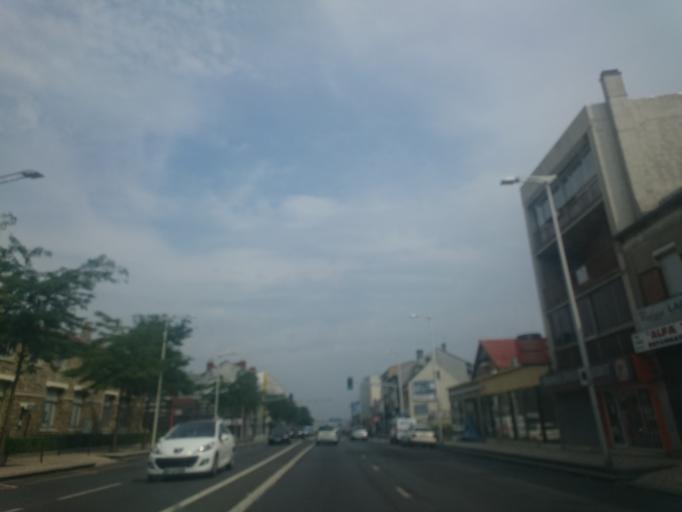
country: FR
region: Ile-de-France
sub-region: Departement de l'Essonne
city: Paray-Vieille-Poste
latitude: 48.7003
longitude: 2.3719
